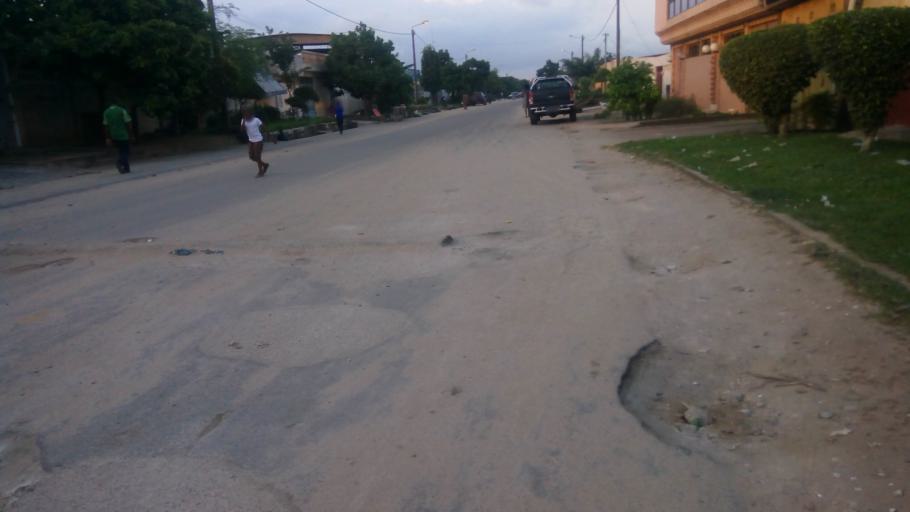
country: CI
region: Lagunes
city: Abobo
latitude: 5.4084
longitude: -3.9913
